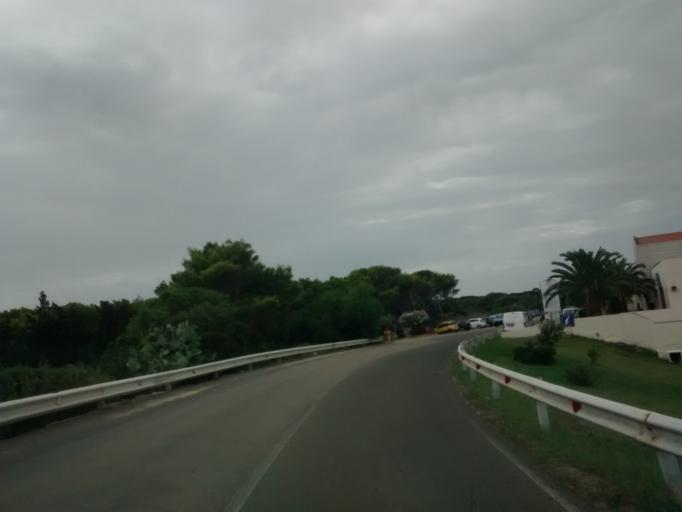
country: IT
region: Sardinia
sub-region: Provincia di Cagliari
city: Villasimius
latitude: 39.1177
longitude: 9.5098
